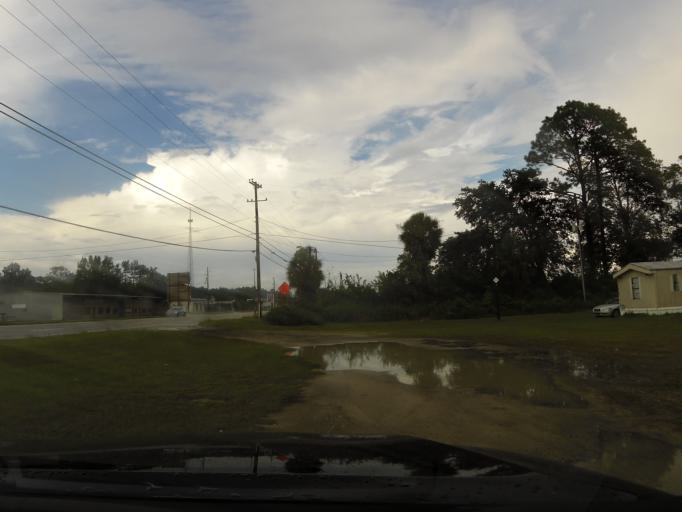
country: US
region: Georgia
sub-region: Wayne County
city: Jesup
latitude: 31.6559
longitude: -81.8510
